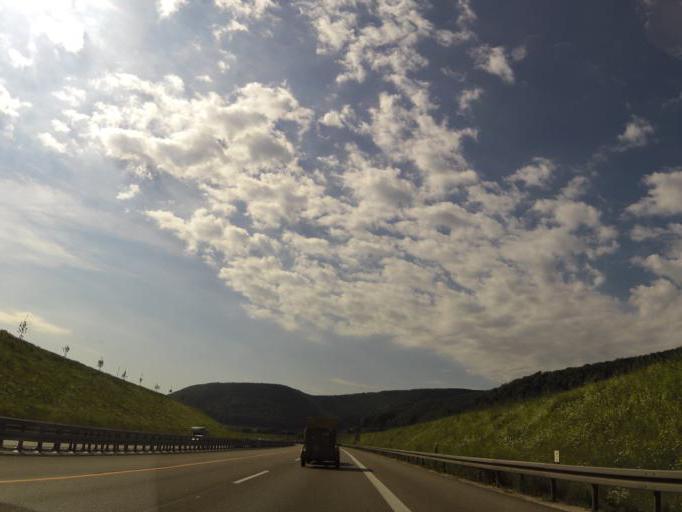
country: DE
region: Baden-Wuerttemberg
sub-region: Regierungsbezirk Stuttgart
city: Gruibingen
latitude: 48.5906
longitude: 9.6504
